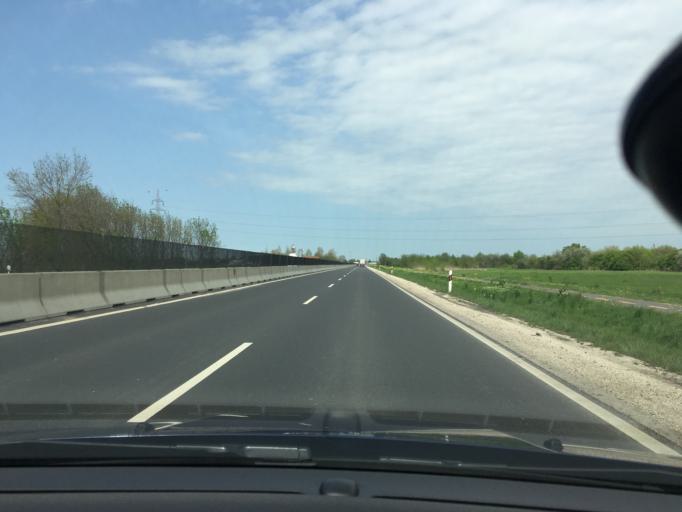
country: HU
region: Csongrad
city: Algyo
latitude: 46.3025
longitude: 20.1809
